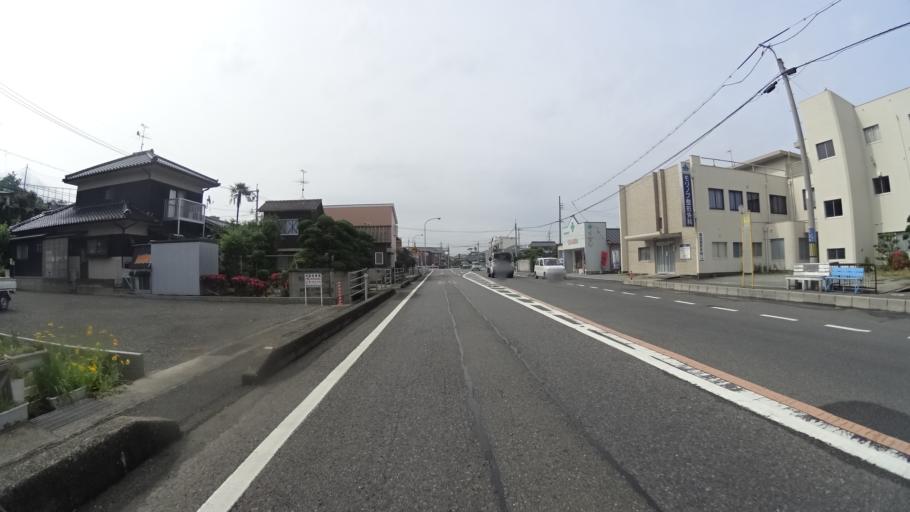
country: JP
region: Yamaguchi
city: Shimonoseki
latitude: 34.0738
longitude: 130.8974
